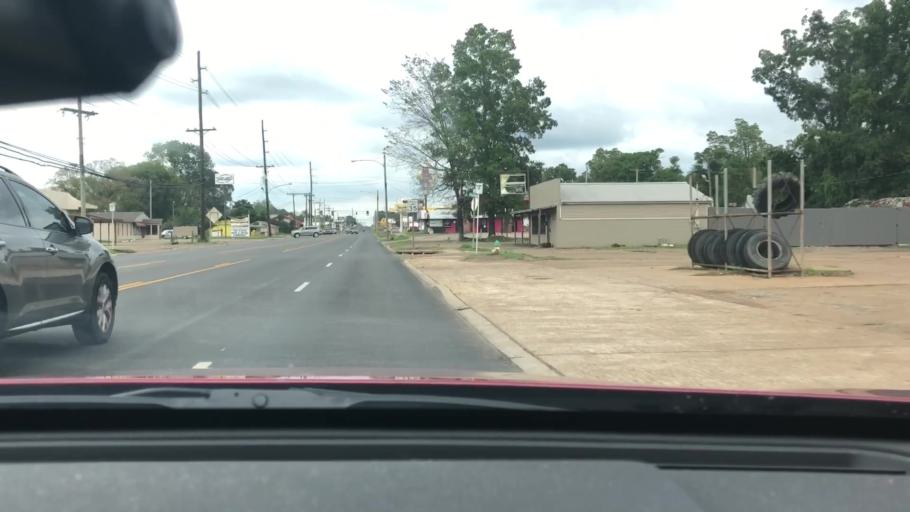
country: US
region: Arkansas
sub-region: Miller County
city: Texarkana
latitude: 33.4307
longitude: -94.0254
